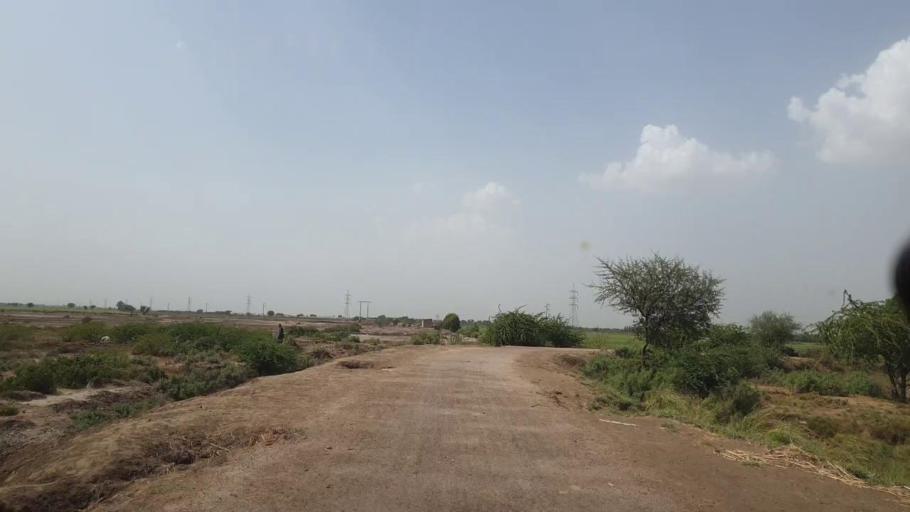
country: PK
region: Sindh
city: Tando Ghulam Ali
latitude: 25.0687
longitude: 68.8115
